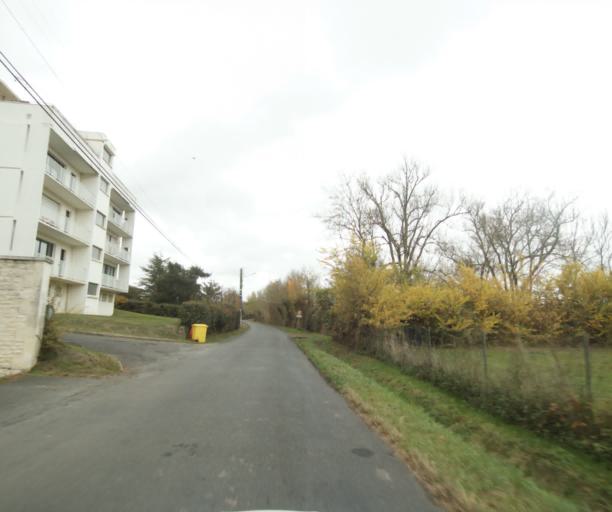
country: FR
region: Poitou-Charentes
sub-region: Departement de la Charente-Maritime
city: Saintes
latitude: 45.7566
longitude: -0.6282
